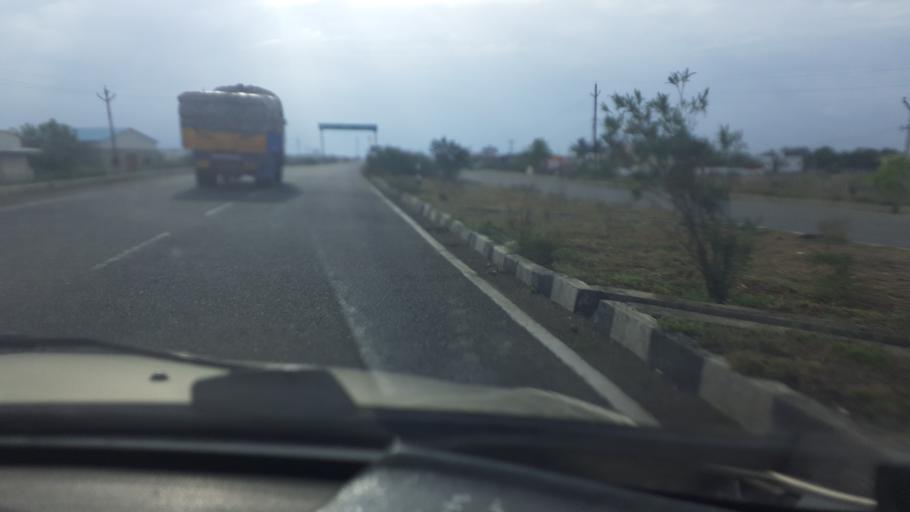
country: IN
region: Tamil Nadu
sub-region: Tirunelveli Kattabo
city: Tirunelveli
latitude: 8.6623
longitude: 77.7242
